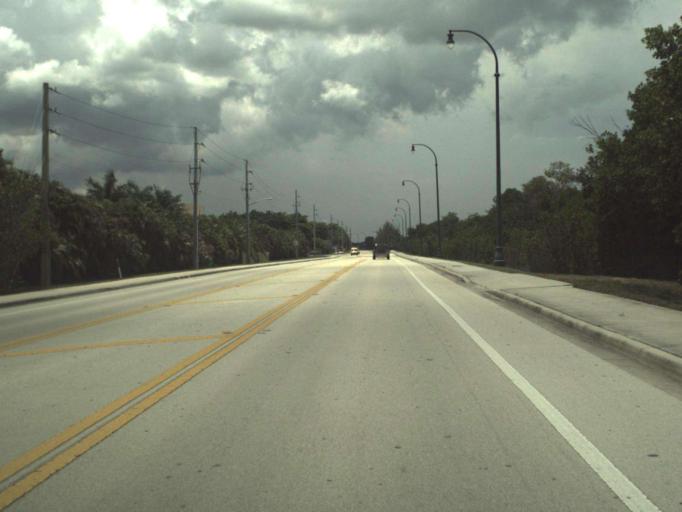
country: US
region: Florida
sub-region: Martin County
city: Jensen Beach
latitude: 27.2557
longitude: -80.2032
